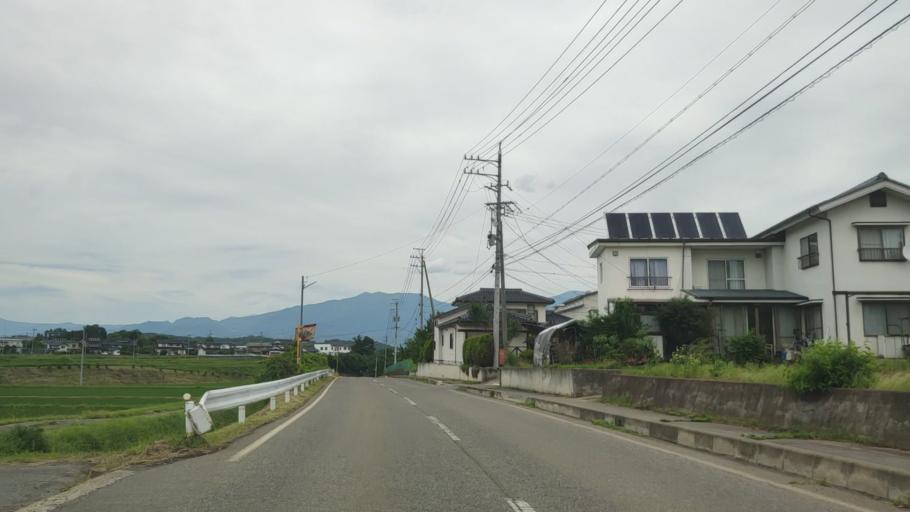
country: JP
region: Nagano
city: Kamimaruko
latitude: 36.2954
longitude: 138.3179
